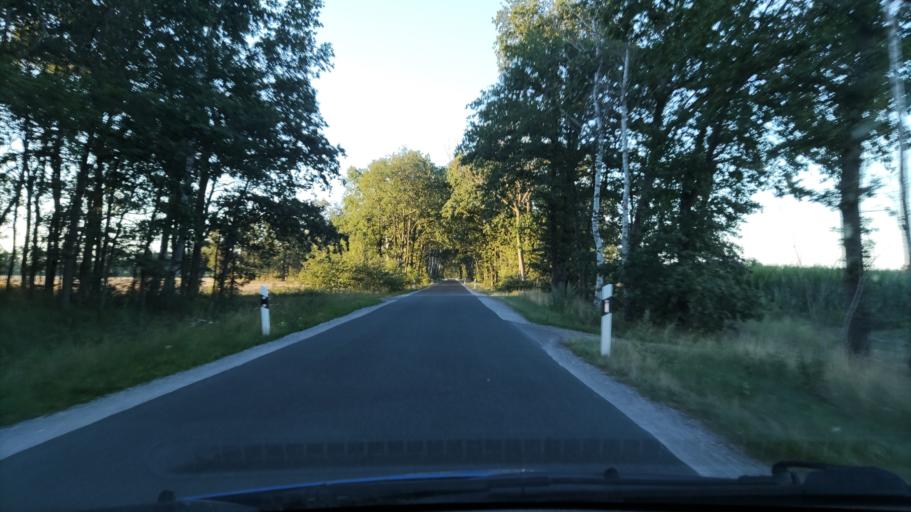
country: DE
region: Lower Saxony
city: Klein Gusborn
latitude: 53.0670
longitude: 11.1878
